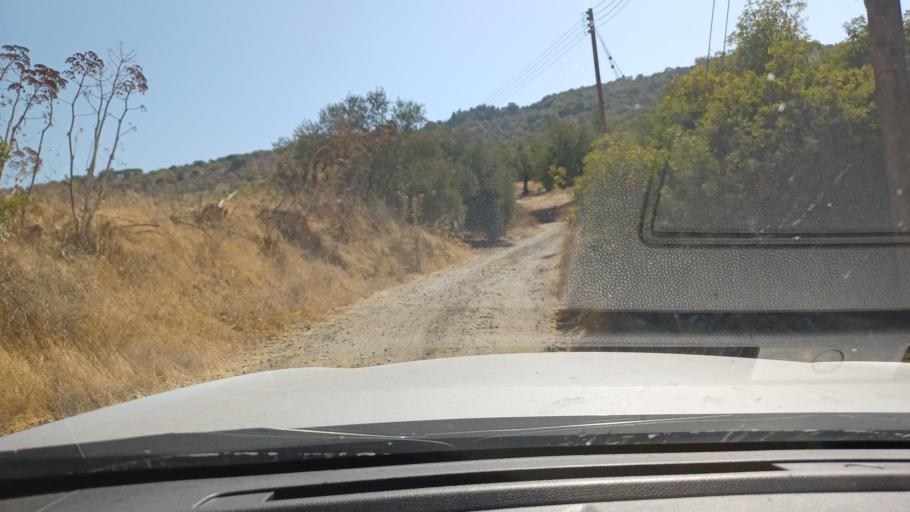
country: CY
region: Pafos
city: Polis
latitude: 35.0005
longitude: 32.4996
